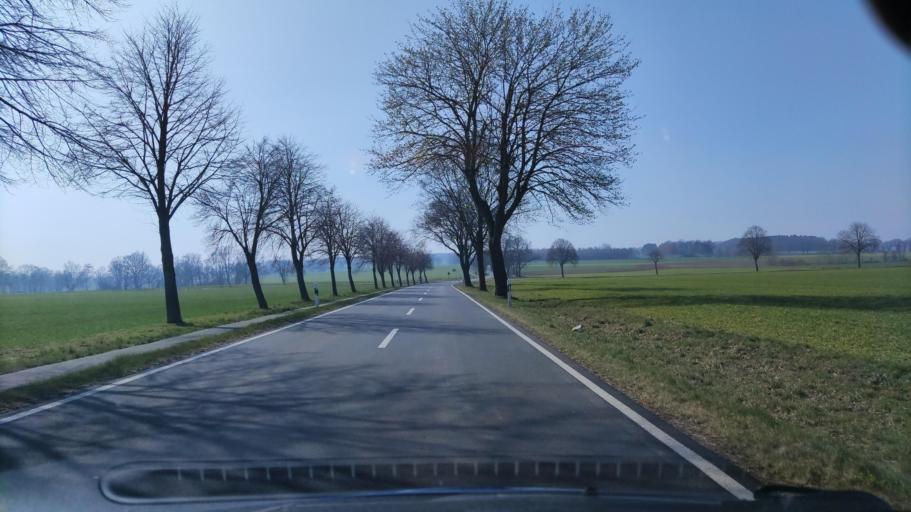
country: DE
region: Lower Saxony
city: Clenze
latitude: 52.9594
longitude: 10.9730
